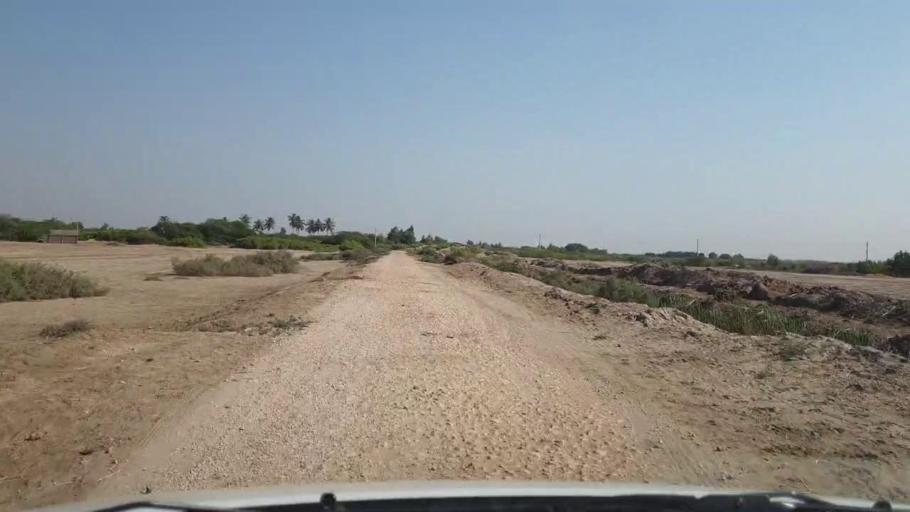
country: PK
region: Sindh
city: Mirpur Sakro
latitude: 24.6475
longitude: 67.6332
